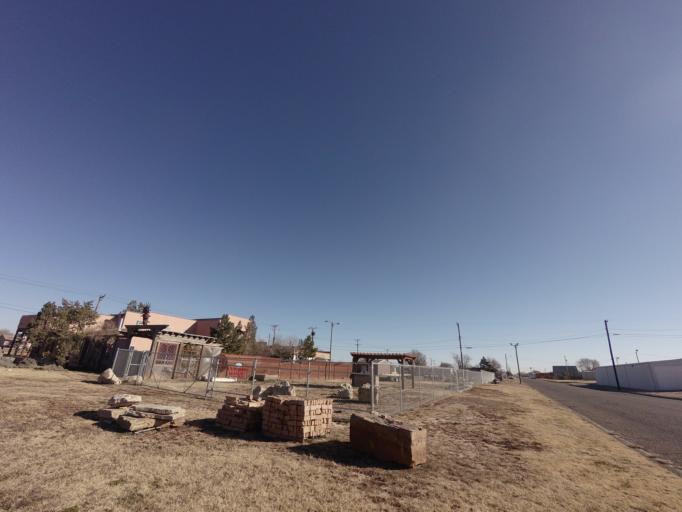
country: US
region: New Mexico
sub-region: Curry County
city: Clovis
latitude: 34.3998
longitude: -103.1939
